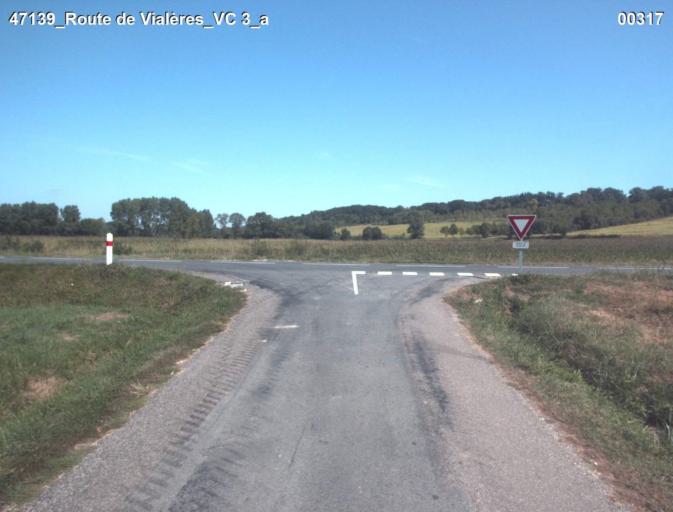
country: FR
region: Aquitaine
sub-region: Departement du Lot-et-Garonne
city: Nerac
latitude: 44.0638
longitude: 0.3845
